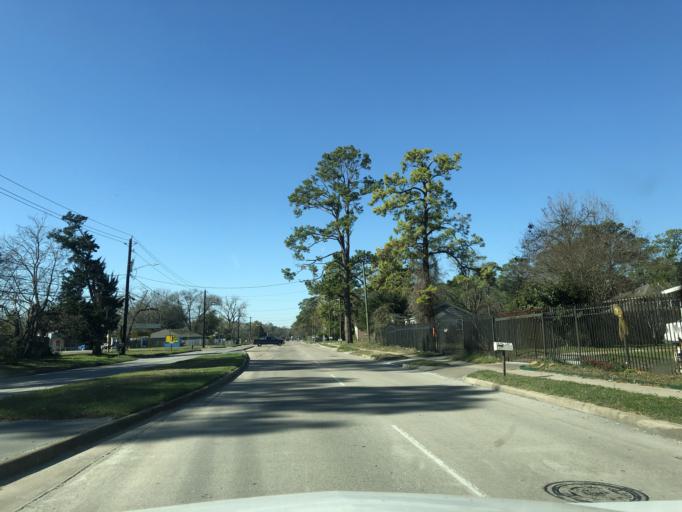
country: US
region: Texas
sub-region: Harris County
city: Jacinto City
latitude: 29.8314
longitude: -95.2968
